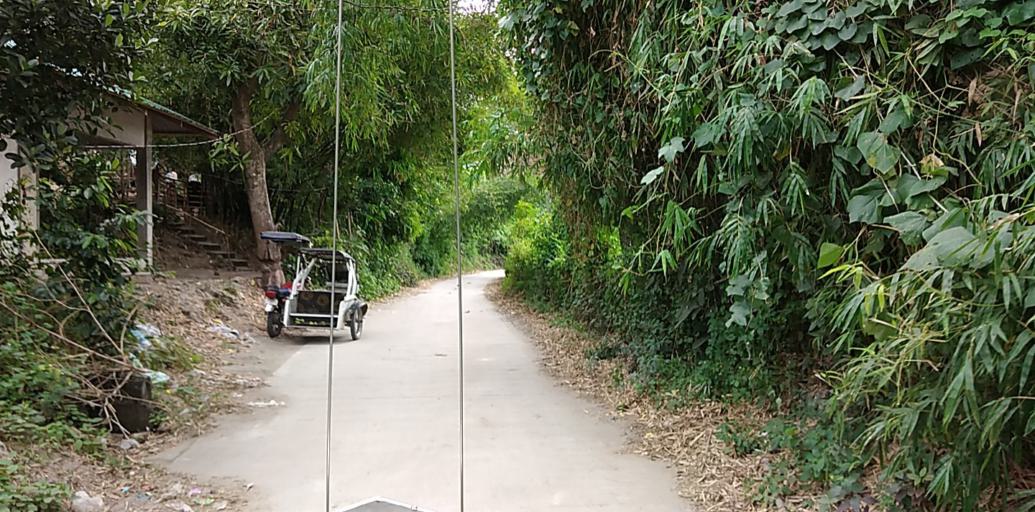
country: PH
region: Central Luzon
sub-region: Province of Pampanga
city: Porac
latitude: 15.0615
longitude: 120.5333
